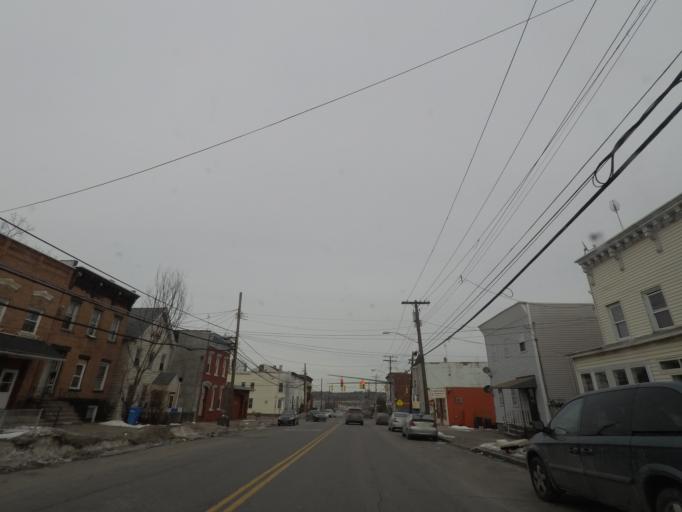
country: US
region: New York
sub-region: Albany County
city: West Albany
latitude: 42.6766
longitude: -73.7823
